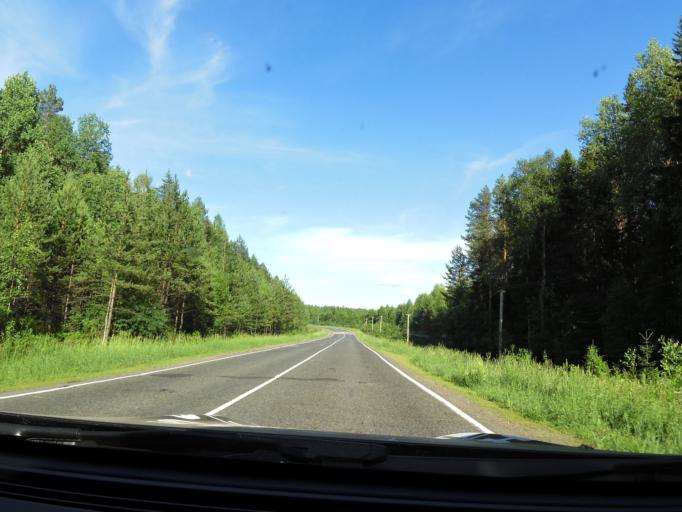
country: RU
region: Kirov
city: Belaya Kholunitsa
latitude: 58.9056
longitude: 51.0291
